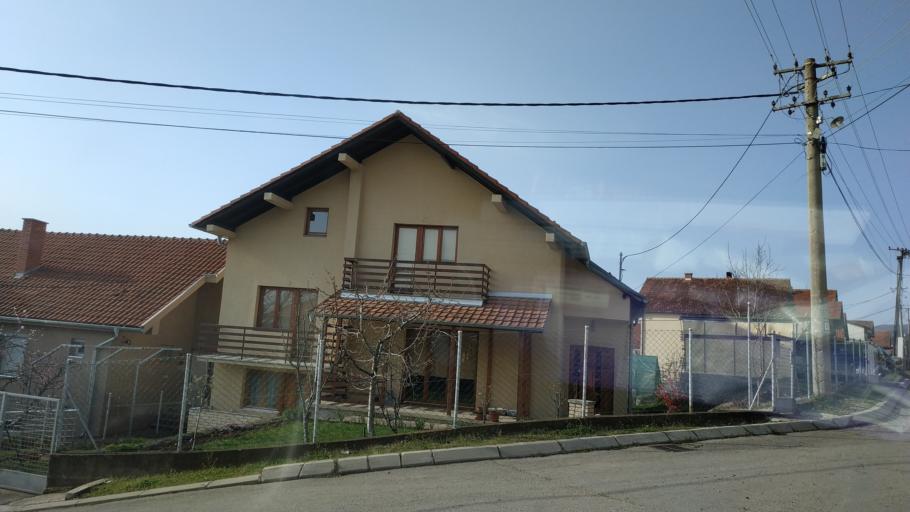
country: RS
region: Central Serbia
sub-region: Nisavski Okrug
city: Aleksinac
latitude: 43.5442
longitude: 21.7170
